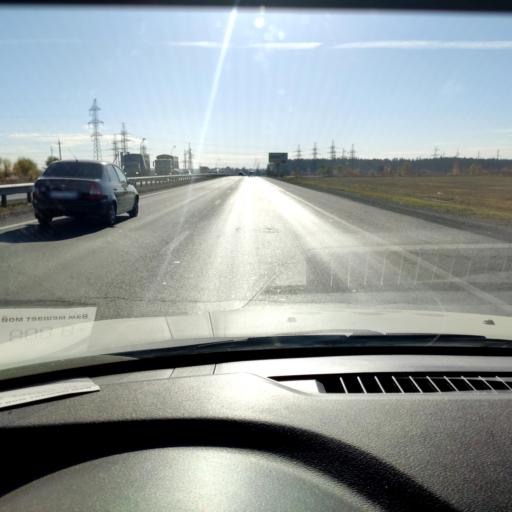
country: RU
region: Samara
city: Zhigulevsk
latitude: 53.5471
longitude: 49.5099
